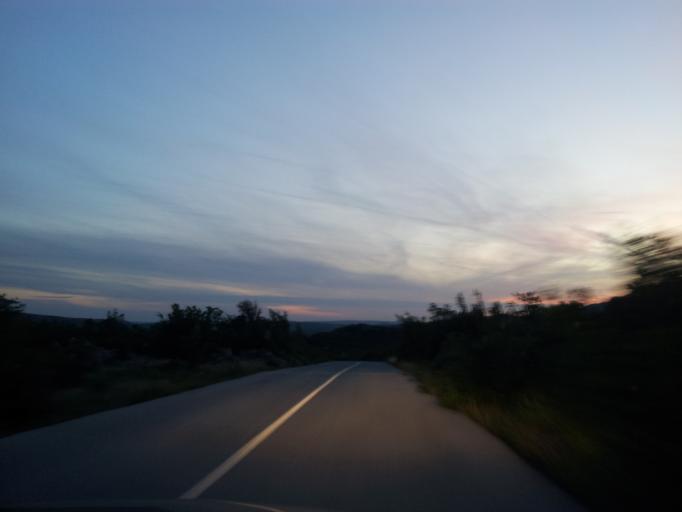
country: HR
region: Zadarska
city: Obrovac
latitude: 44.2265
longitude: 15.6713
